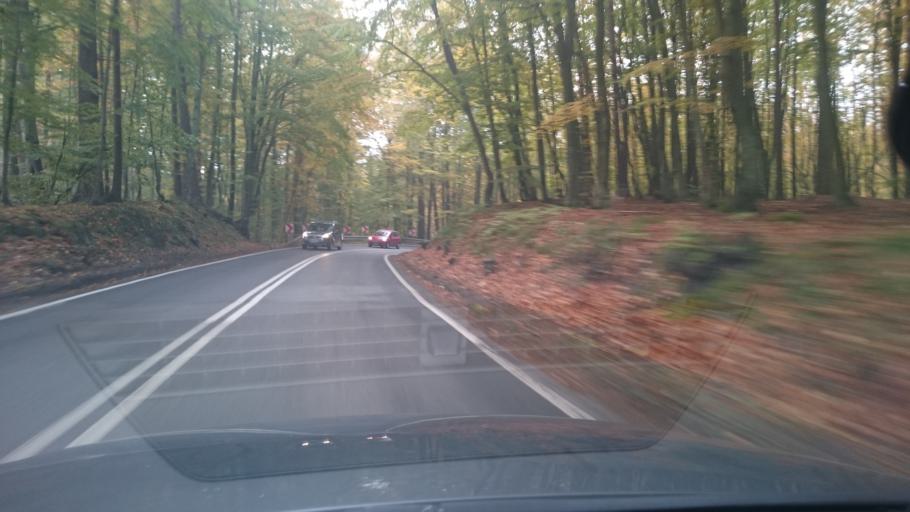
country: PL
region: Pomeranian Voivodeship
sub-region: Gdynia
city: Wielki Kack
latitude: 54.4601
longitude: 18.5089
